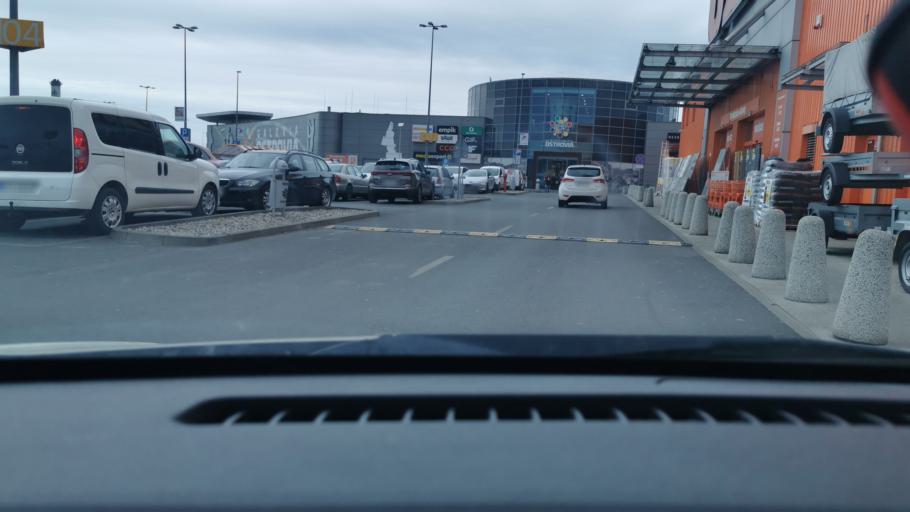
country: PL
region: Greater Poland Voivodeship
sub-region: Powiat ostrowski
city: Ostrow Wielkopolski
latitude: 51.6566
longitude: 17.8463
